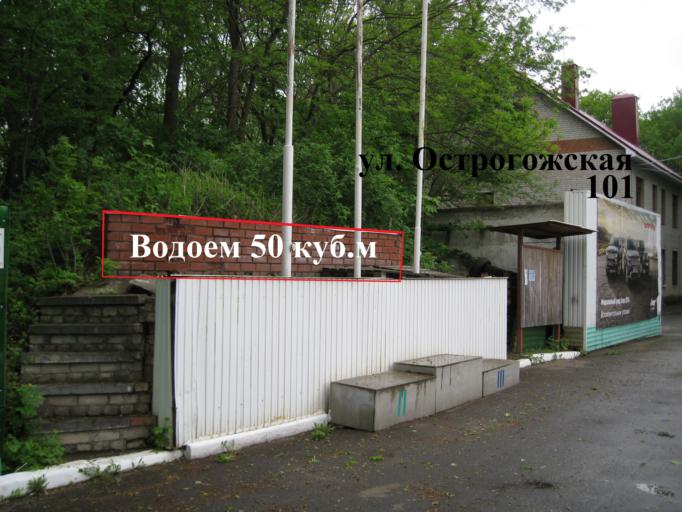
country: RU
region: Voronezj
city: Voronezh
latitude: 51.6192
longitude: 39.1811
